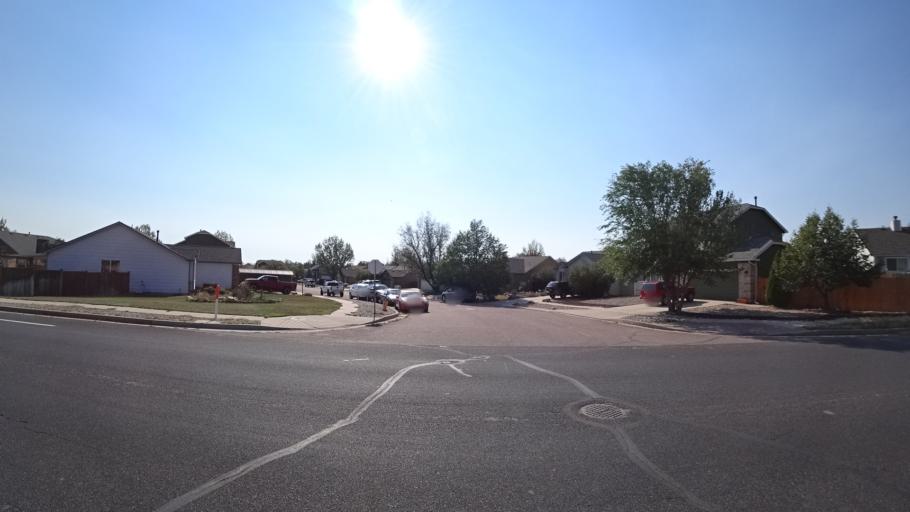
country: US
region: Colorado
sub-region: El Paso County
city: Stratmoor
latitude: 38.7703
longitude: -104.8009
